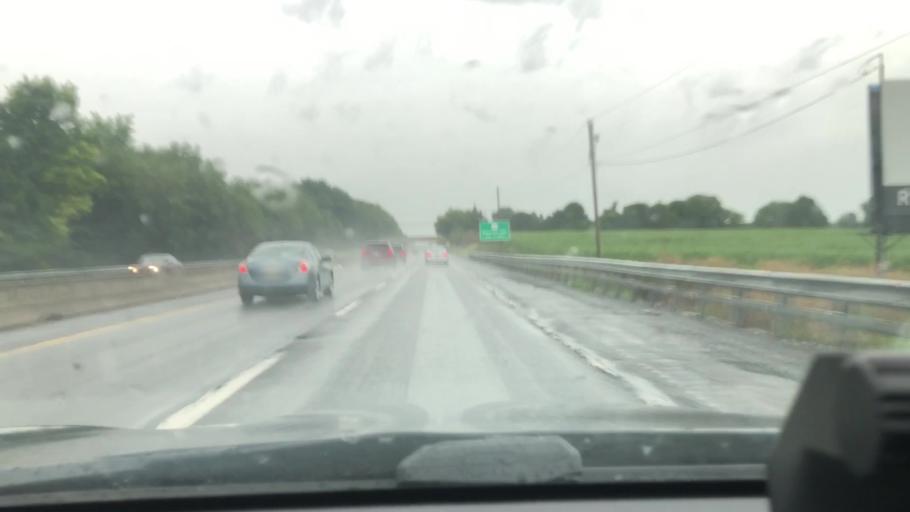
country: US
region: Pennsylvania
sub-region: Northampton County
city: Middletown
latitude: 40.6809
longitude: -75.3257
